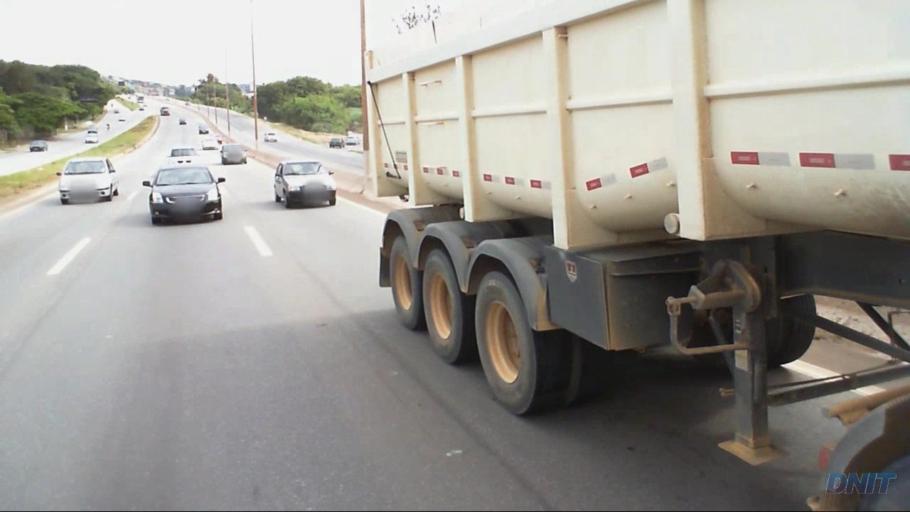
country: BR
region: Minas Gerais
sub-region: Belo Horizonte
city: Belo Horizonte
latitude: -19.8613
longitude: -43.9205
